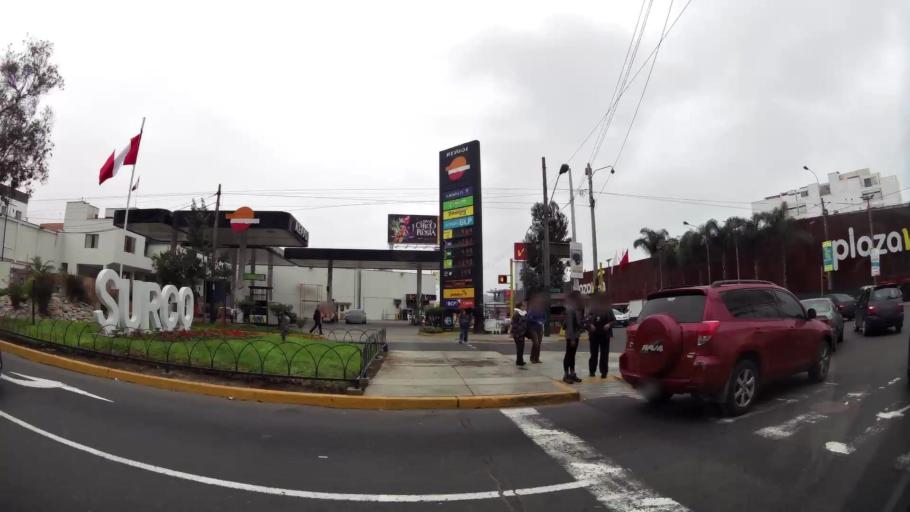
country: PE
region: Lima
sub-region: Lima
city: Surco
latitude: -12.1336
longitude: -77.0177
